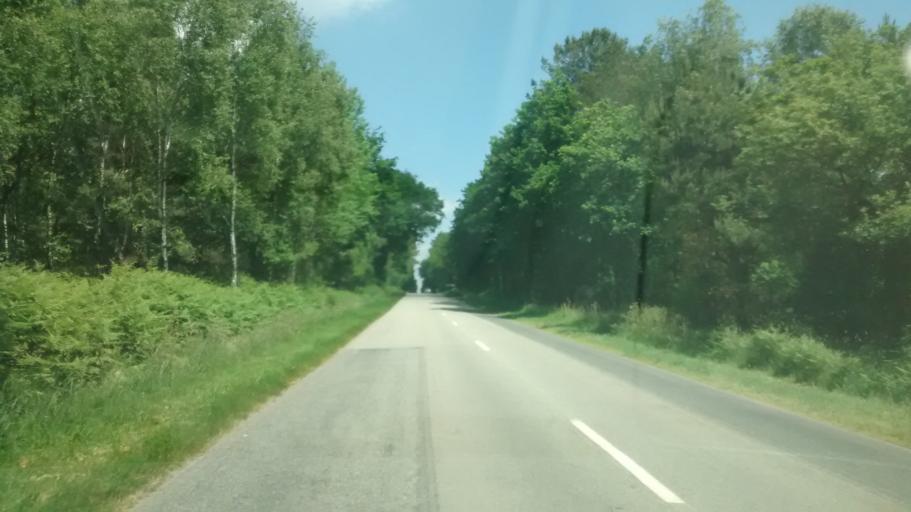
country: FR
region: Brittany
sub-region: Departement du Morbihan
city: Guer
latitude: 47.8823
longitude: -2.1866
